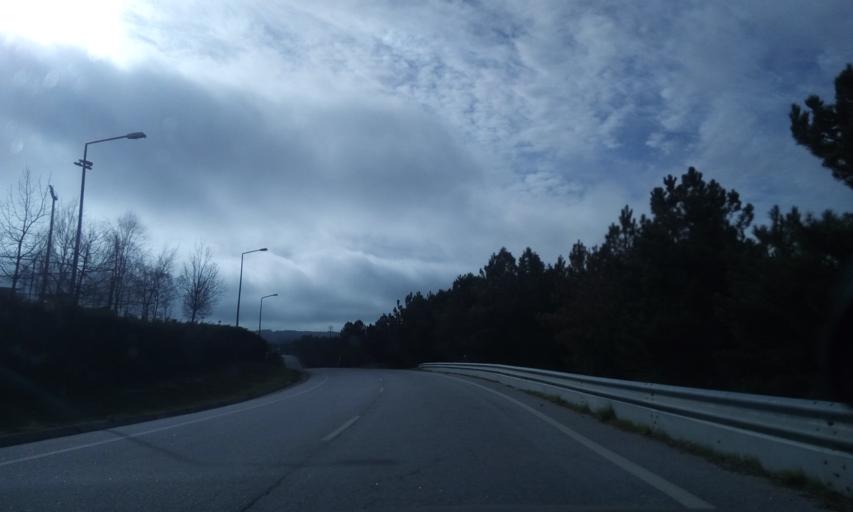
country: PT
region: Guarda
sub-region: Aguiar da Beira
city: Aguiar da Beira
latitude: 40.8137
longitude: -7.5364
